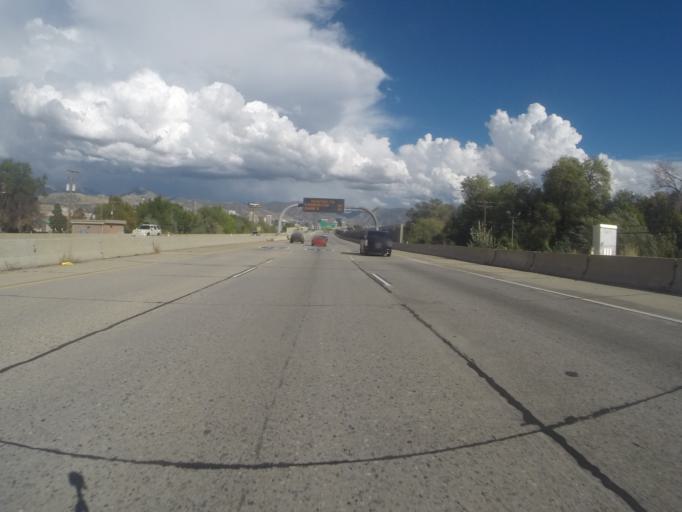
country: US
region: Utah
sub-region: Salt Lake County
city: Salt Lake City
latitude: 40.7645
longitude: -111.9268
